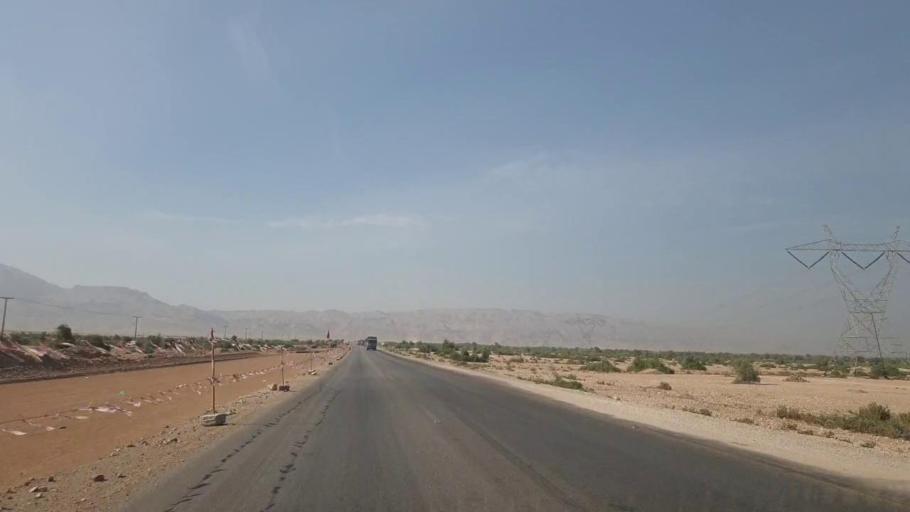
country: PK
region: Sindh
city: Sehwan
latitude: 26.2122
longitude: 67.9210
